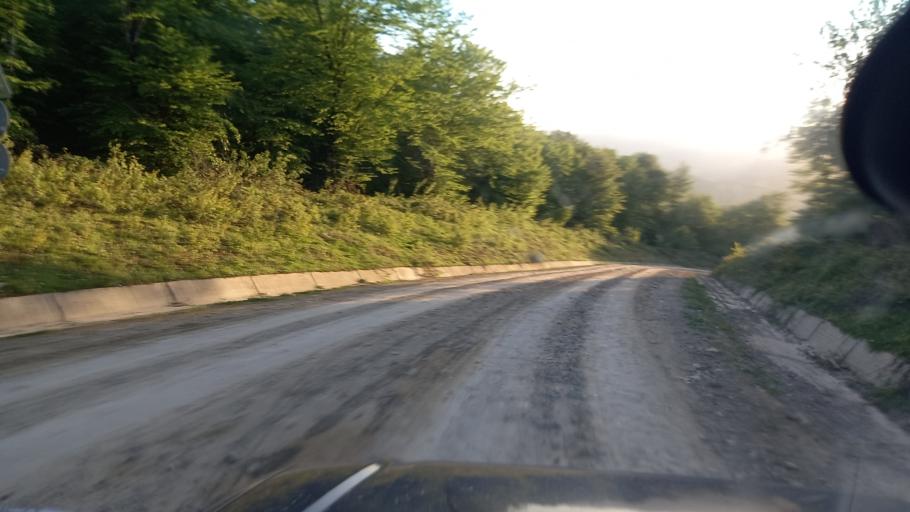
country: RU
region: Dagestan
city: Khuchni
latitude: 42.0038
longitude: 47.9740
